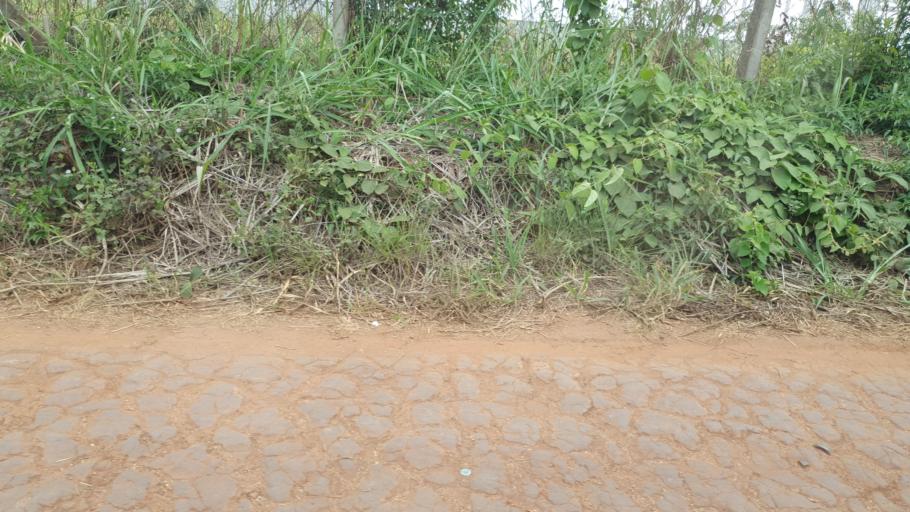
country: BR
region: Sao Paulo
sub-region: Sorocaba
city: Sorocaba
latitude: -23.4545
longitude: -47.4080
